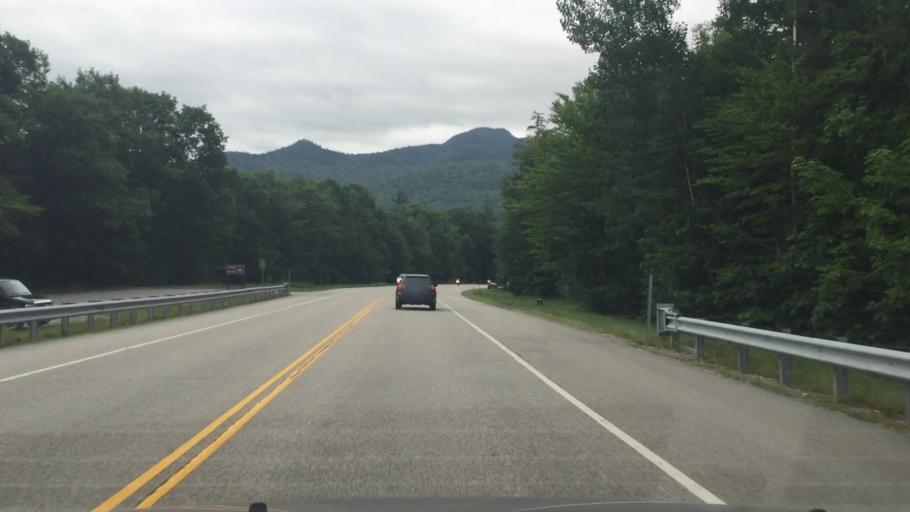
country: US
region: New Hampshire
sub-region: Carroll County
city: North Conway
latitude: 44.0848
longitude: -71.3493
